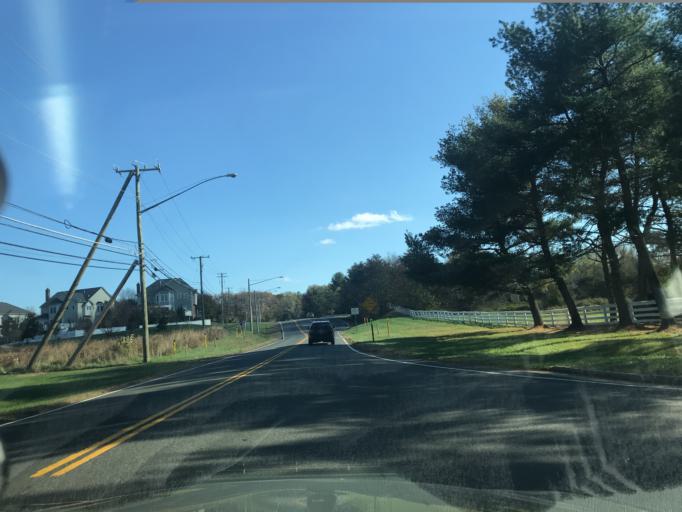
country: US
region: Virginia
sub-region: Fairfax County
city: Oak Hill
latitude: 38.9149
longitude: -77.3881
